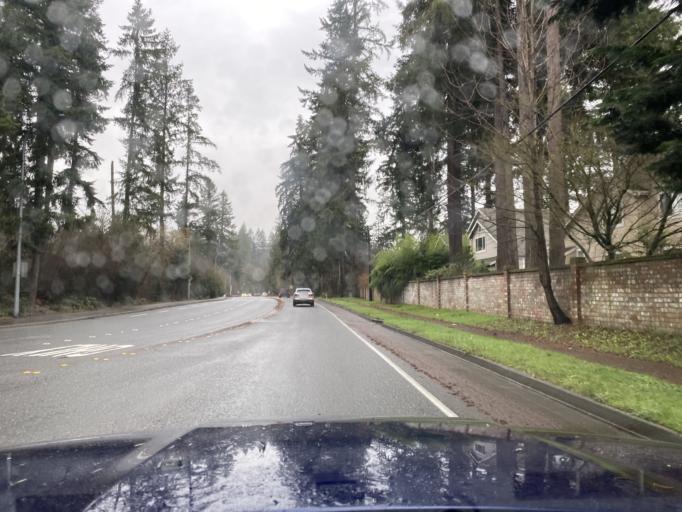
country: US
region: Washington
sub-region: King County
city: Redmond
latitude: 47.6873
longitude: -122.0929
